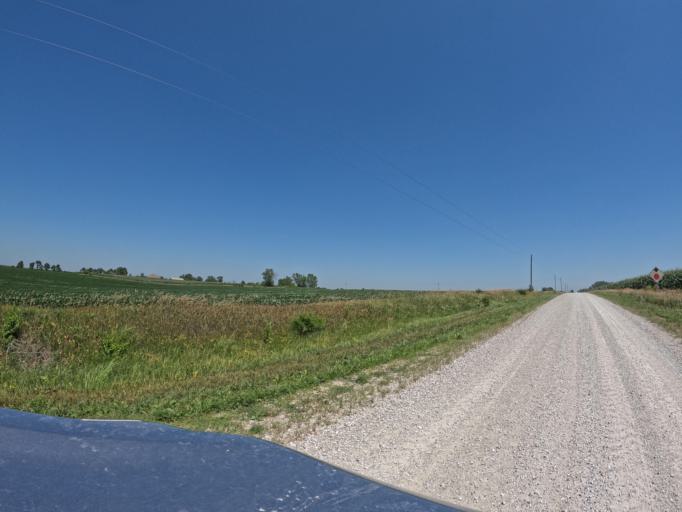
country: US
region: Iowa
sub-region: Keokuk County
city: Sigourney
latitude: 41.4234
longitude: -92.3576
